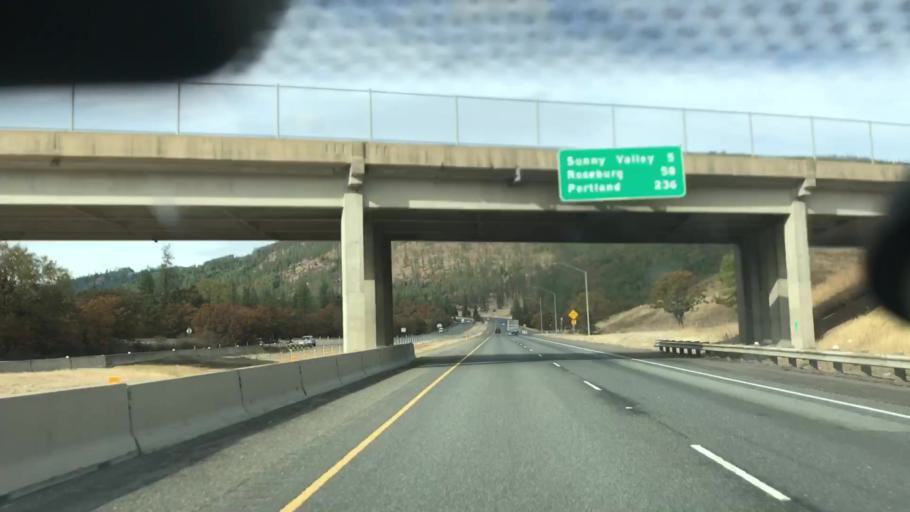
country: US
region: Oregon
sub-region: Josephine County
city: Merlin
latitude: 42.5664
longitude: -123.3721
